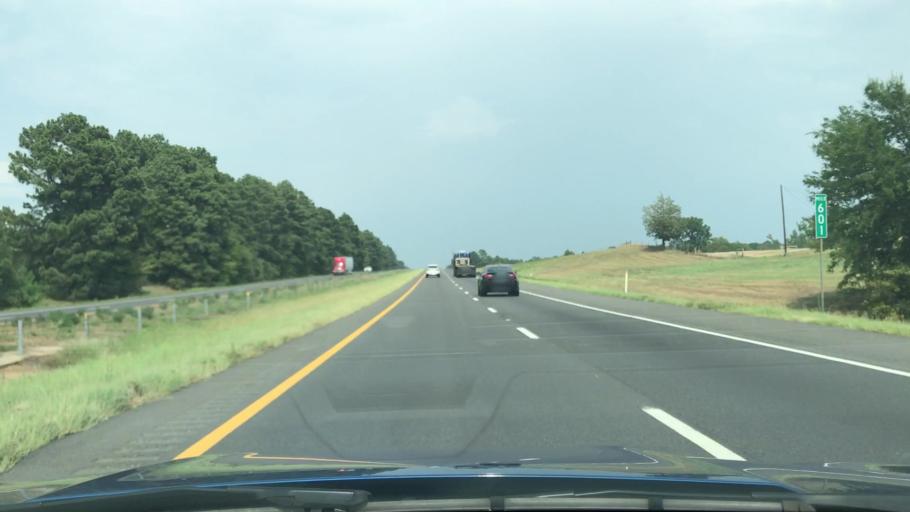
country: US
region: Texas
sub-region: Harrison County
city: Hallsville
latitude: 32.4648
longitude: -94.6345
